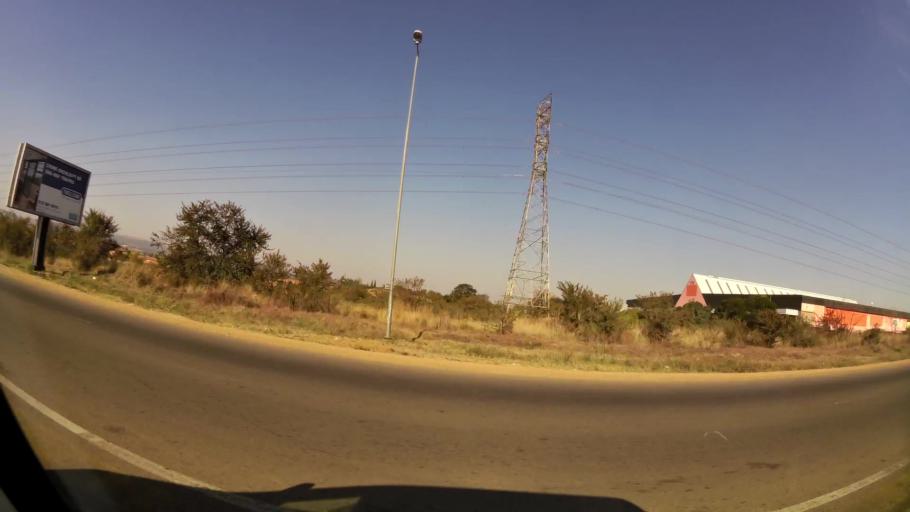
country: ZA
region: Gauteng
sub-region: City of Tshwane Metropolitan Municipality
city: Pretoria
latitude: -25.7690
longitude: 28.3553
